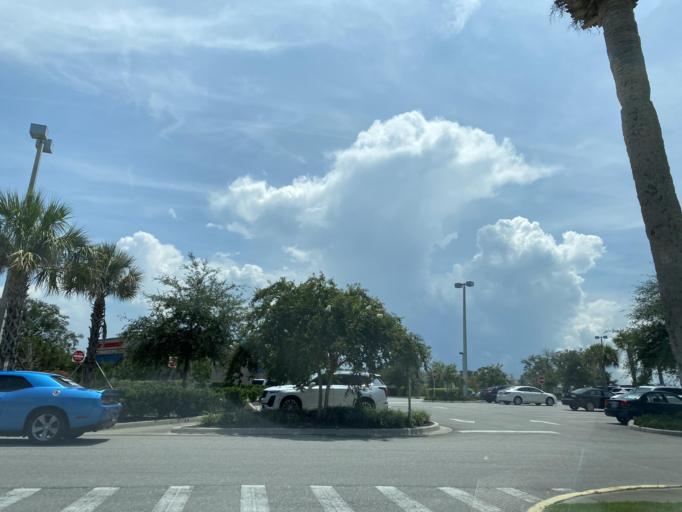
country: US
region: Florida
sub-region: Flagler County
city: Palm Coast
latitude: 29.5578
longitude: -81.2082
